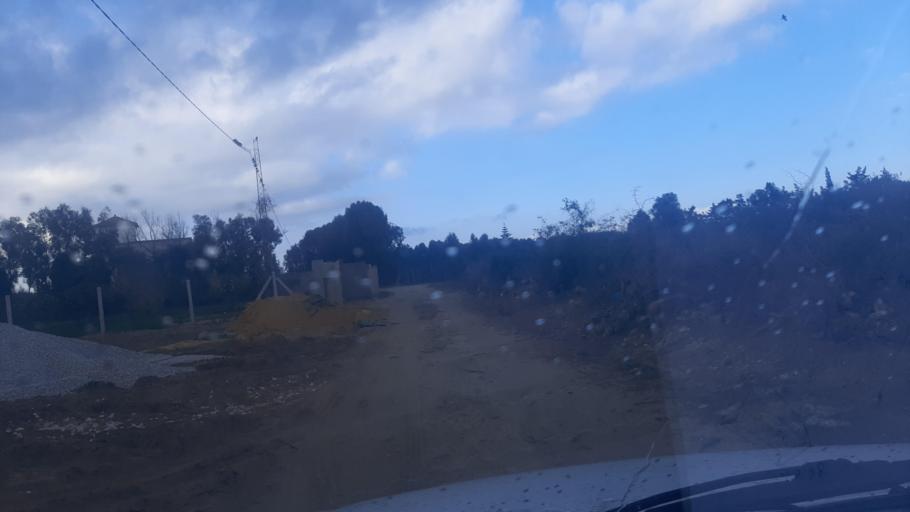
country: TN
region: Nabul
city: Qurbus
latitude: 36.7447
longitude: 10.5261
